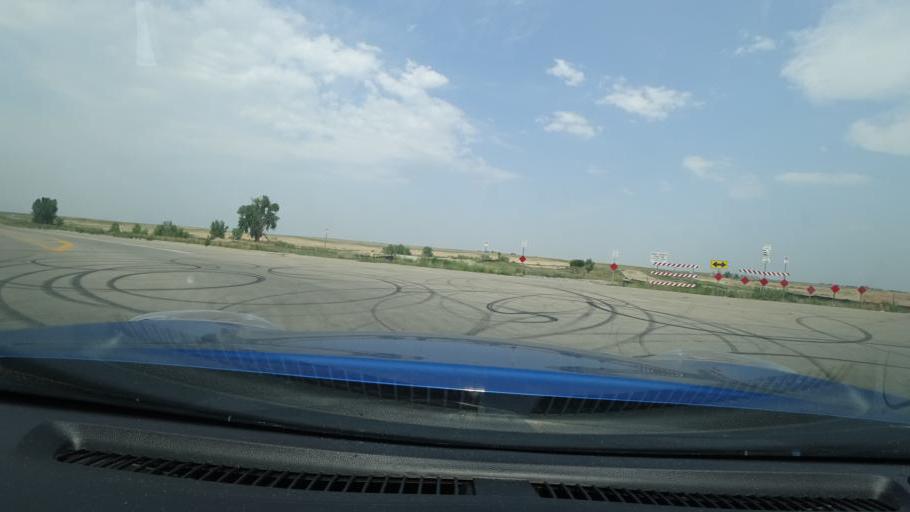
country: US
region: Colorado
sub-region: Adams County
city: Aurora
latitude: 39.7818
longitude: -104.7348
